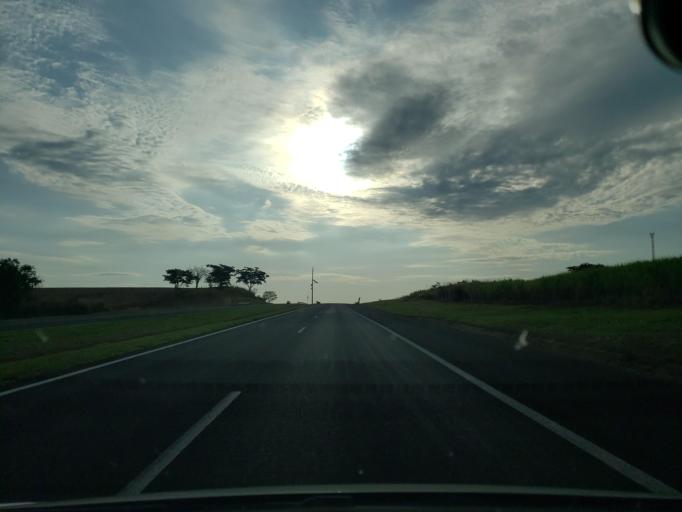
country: BR
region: Sao Paulo
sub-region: Mirandopolis
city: Mirandopolis
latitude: -21.1099
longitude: -51.0251
